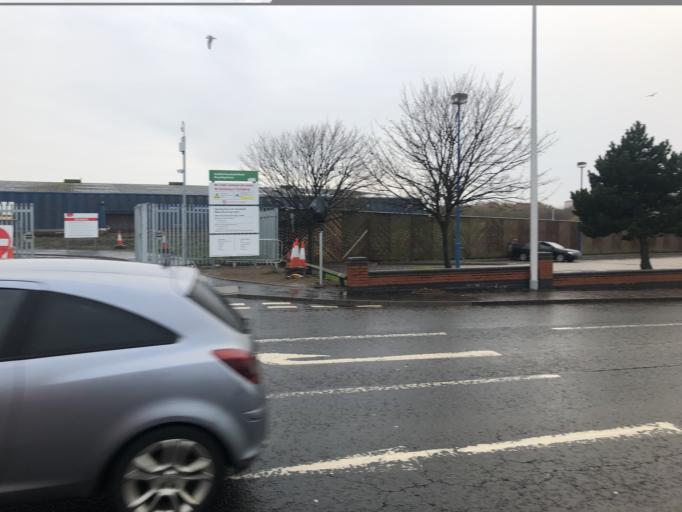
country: GB
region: Scotland
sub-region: West Lothian
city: Seafield
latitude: 55.9682
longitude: -3.1382
